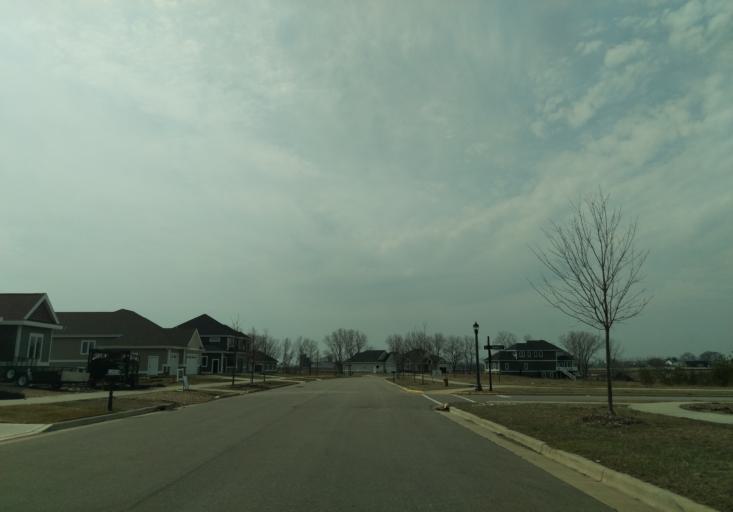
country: US
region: Wisconsin
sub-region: Dane County
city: Waunakee
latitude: 43.1707
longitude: -89.4530
